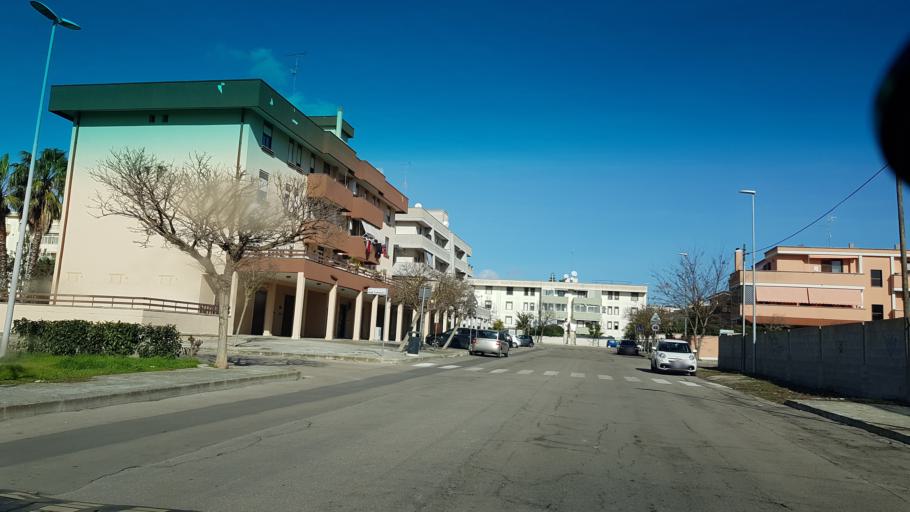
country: IT
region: Apulia
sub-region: Provincia di Lecce
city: Lecce
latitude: 40.3468
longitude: 18.1510
